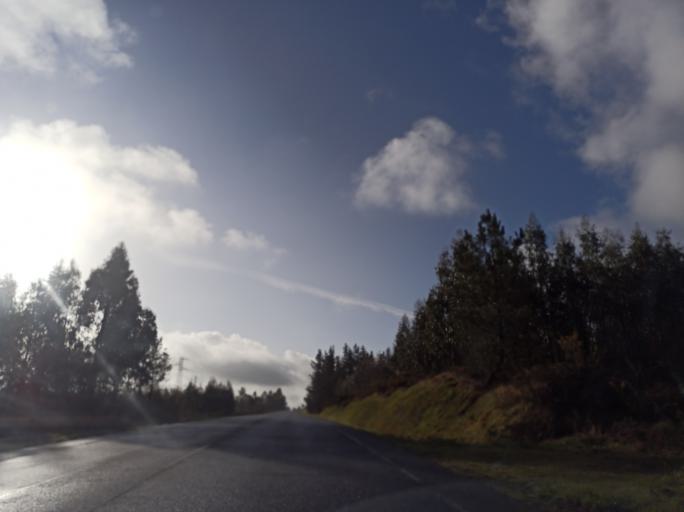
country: ES
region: Galicia
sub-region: Provincia da Coruna
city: Curtis
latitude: 43.1229
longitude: -8.0300
